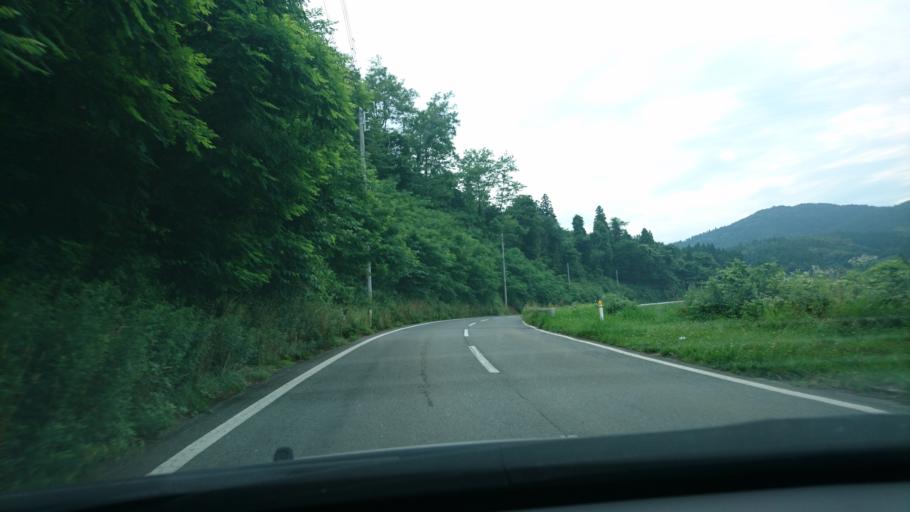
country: JP
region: Iwate
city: Ichinoseki
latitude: 38.8943
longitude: 141.4257
